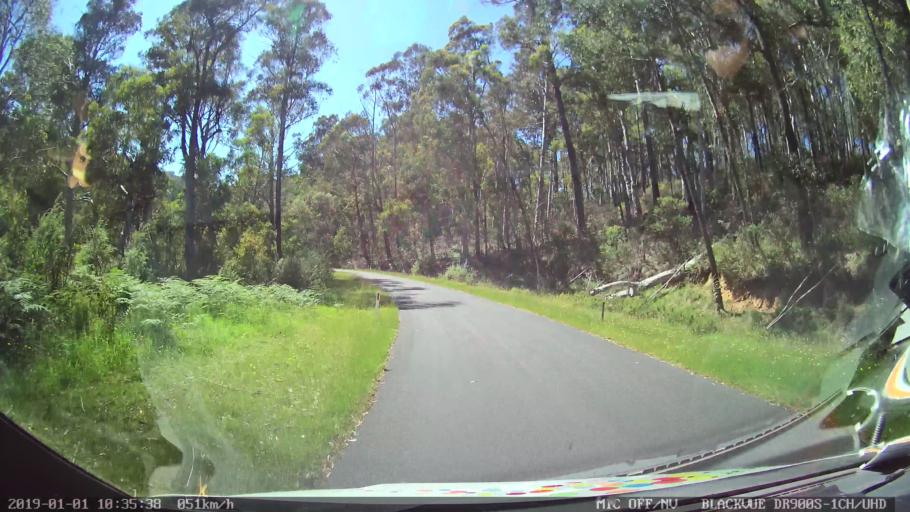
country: AU
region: New South Wales
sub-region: Snowy River
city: Jindabyne
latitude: -36.0487
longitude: 148.2899
